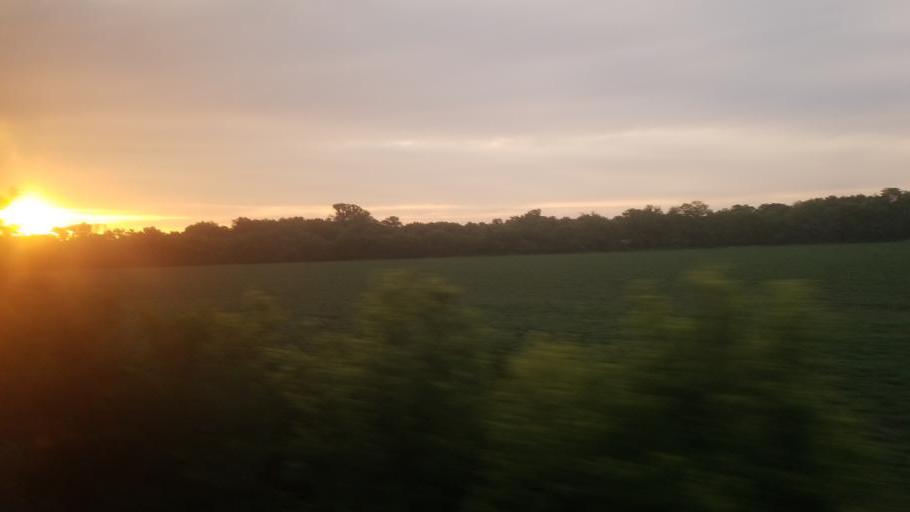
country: US
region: Kansas
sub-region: Marion County
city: Peabody
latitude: 38.1558
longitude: -97.1186
